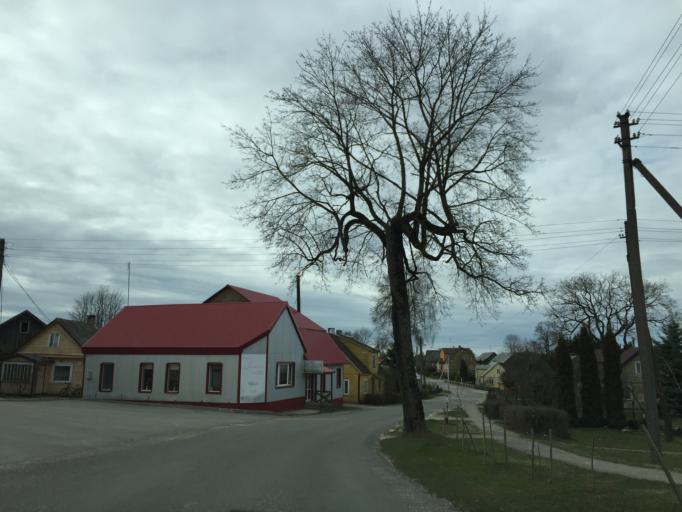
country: LT
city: Silale
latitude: 55.6199
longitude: 22.2323
